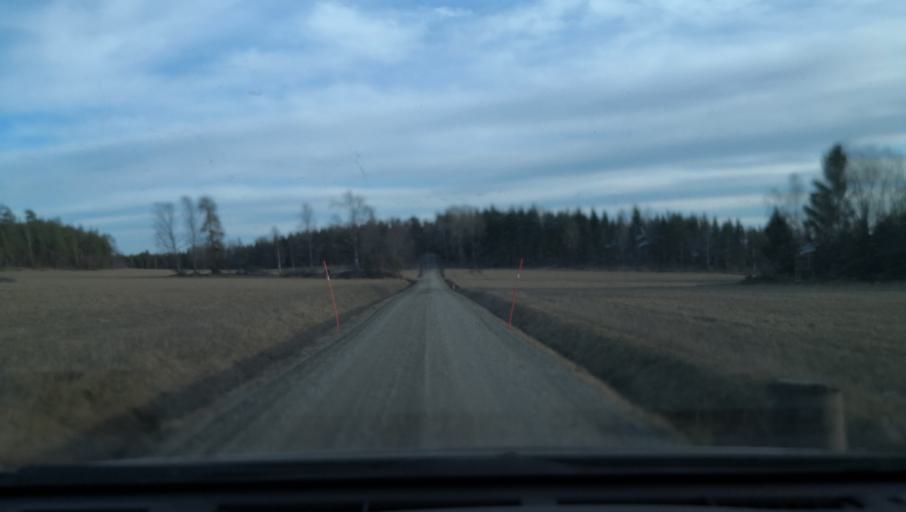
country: SE
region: Uppsala
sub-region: Enkopings Kommun
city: Dalby
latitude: 59.4841
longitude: 17.2502
